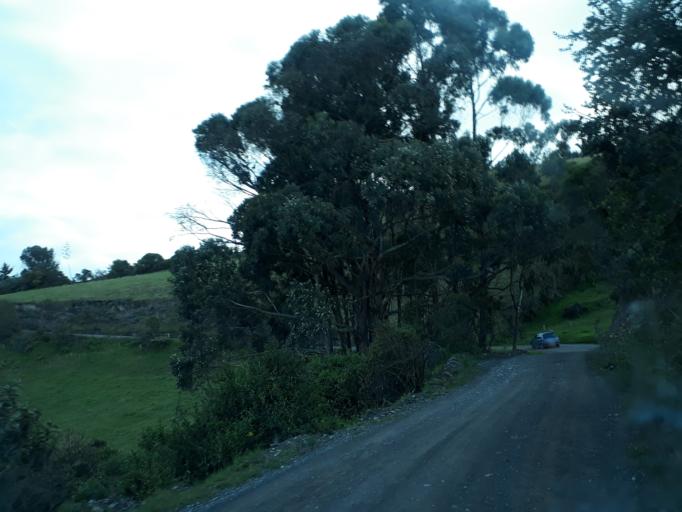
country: CO
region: Cundinamarca
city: Carmen de Carupa
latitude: 5.3431
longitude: -73.9055
